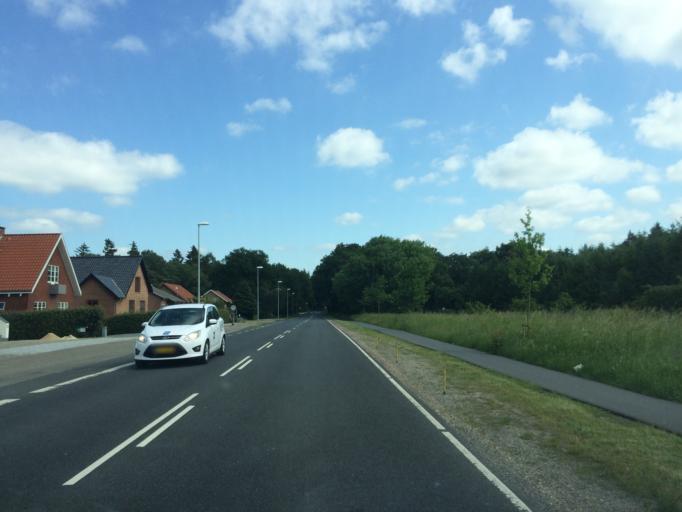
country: DK
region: Central Jutland
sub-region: Silkeborg Kommune
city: Silkeborg
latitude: 56.1587
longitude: 9.5159
